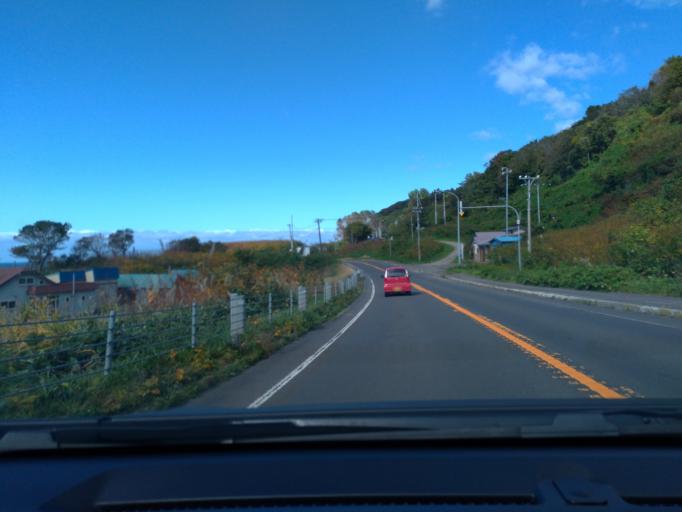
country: JP
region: Hokkaido
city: Ishikari
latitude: 43.4219
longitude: 141.4287
